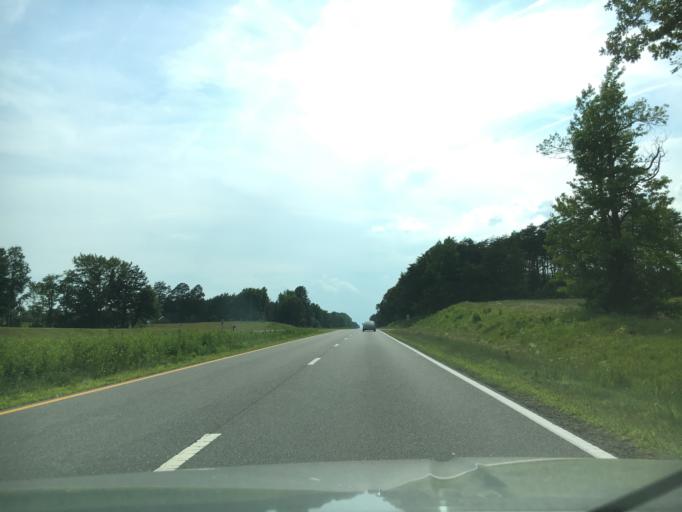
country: US
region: Virginia
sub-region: Halifax County
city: Halifax
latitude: 36.8244
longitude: -78.7038
